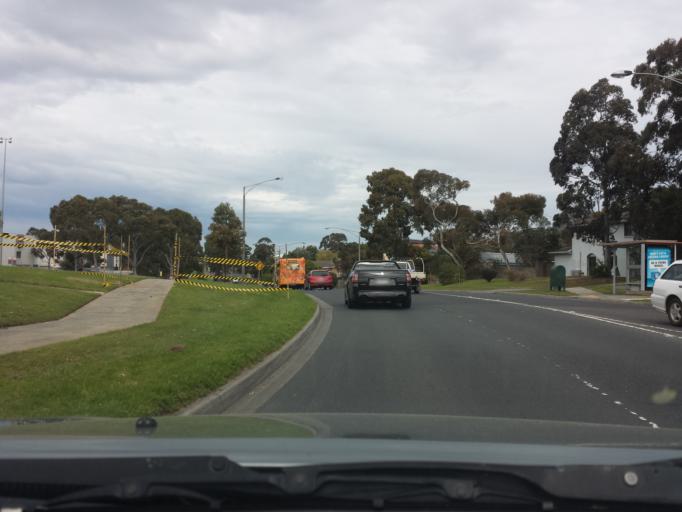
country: AU
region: Victoria
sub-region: Casey
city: Endeavour Hills
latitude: -37.9754
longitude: 145.2581
